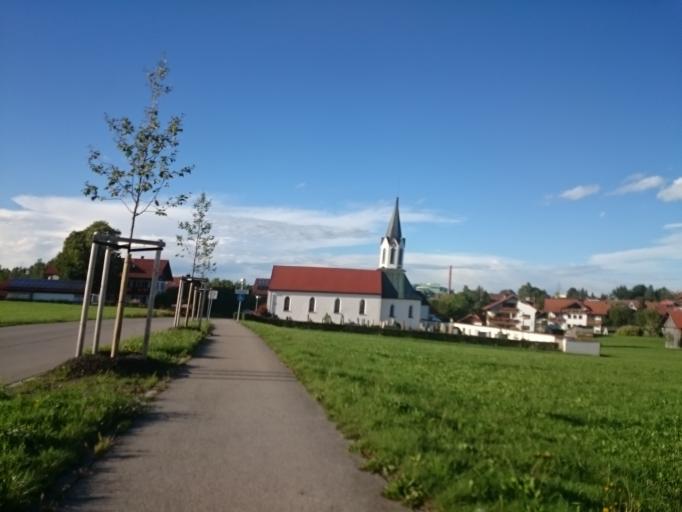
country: DE
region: Bavaria
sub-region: Swabia
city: Kempten (Allgaeu)
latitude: 47.7512
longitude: 10.3189
